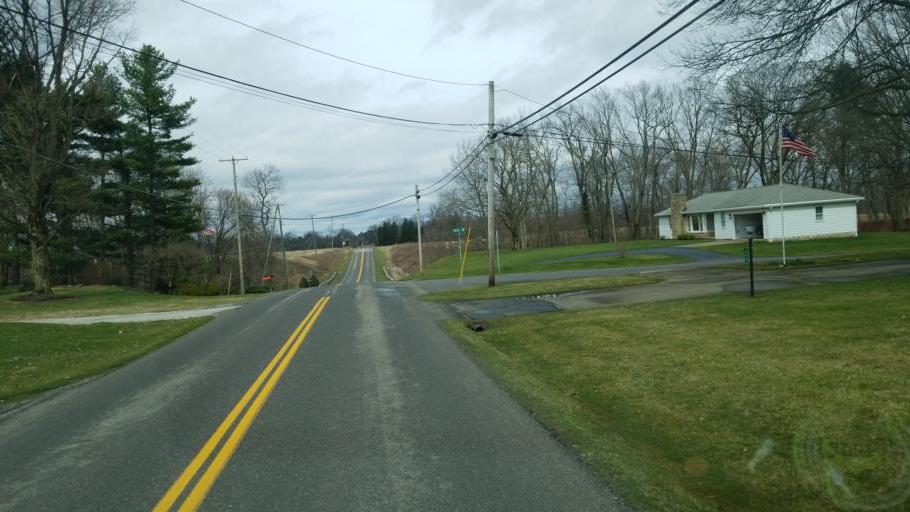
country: US
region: Ohio
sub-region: Wayne County
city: Wooster
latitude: 40.7691
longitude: -81.9632
